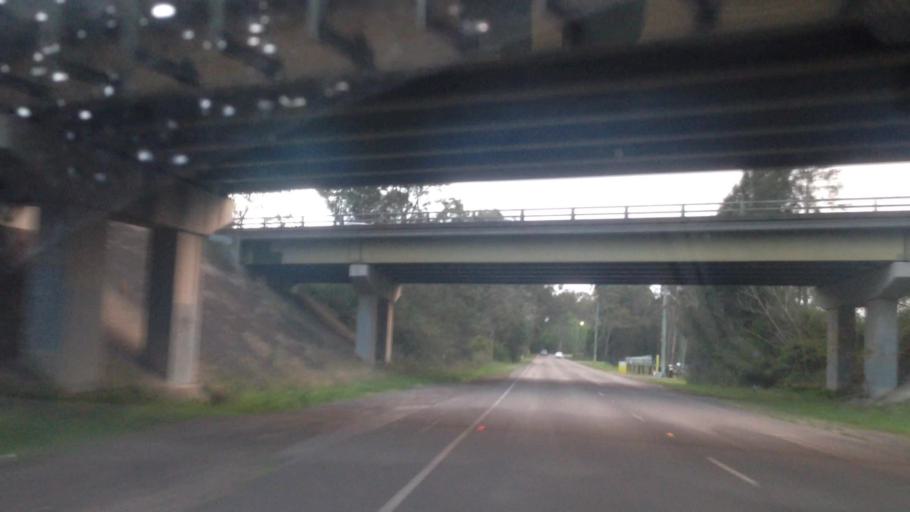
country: AU
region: New South Wales
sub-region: Lake Macquarie Shire
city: Cooranbong
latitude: -33.0939
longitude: 151.4671
